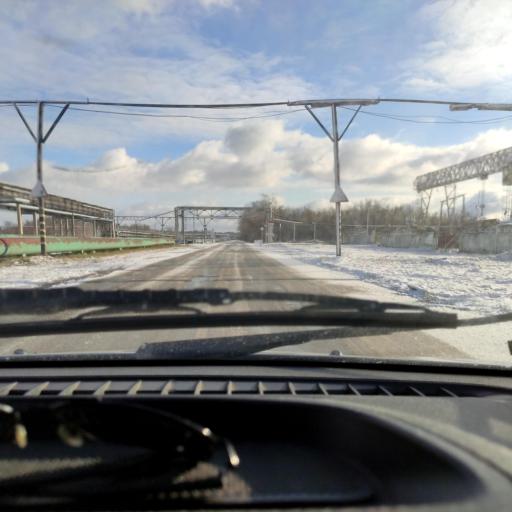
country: RU
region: Samara
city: Tol'yatti
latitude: 53.5358
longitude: 49.4724
